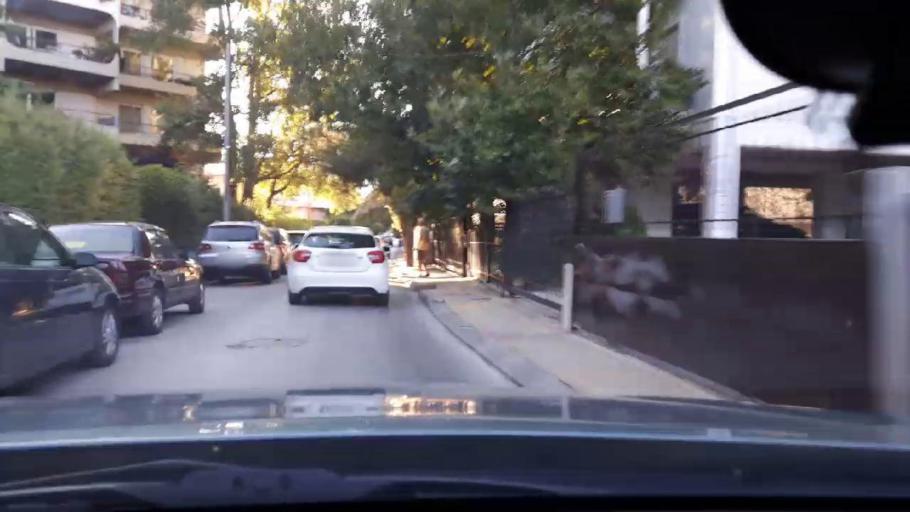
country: GR
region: Attica
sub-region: Nomarchia Athinas
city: Melissia
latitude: 38.0497
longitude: 23.8331
